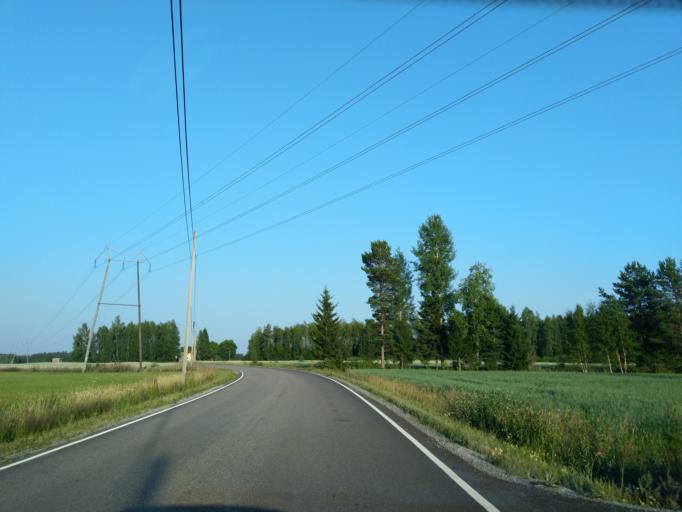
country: FI
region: Satakunta
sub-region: Pohjois-Satakunta
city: Kankaanpaeae
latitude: 61.8185
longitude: 22.3315
